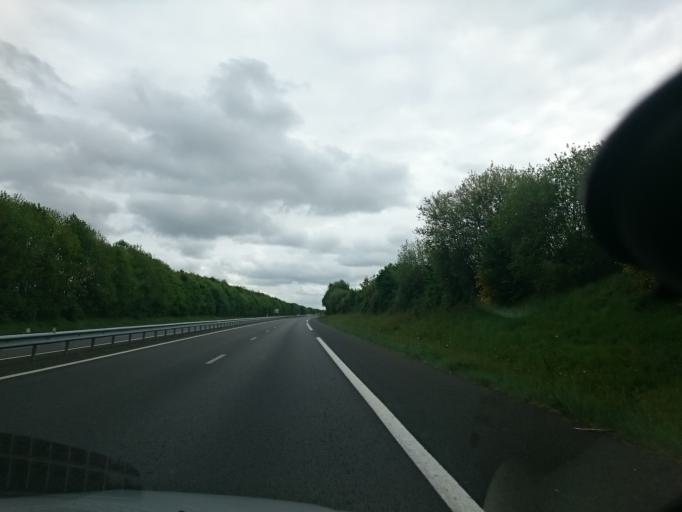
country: FR
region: Brittany
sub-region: Departement d'Ille-et-Vilaine
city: Saint-Etienne-en-Cogles
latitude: 48.3791
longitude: -1.3038
